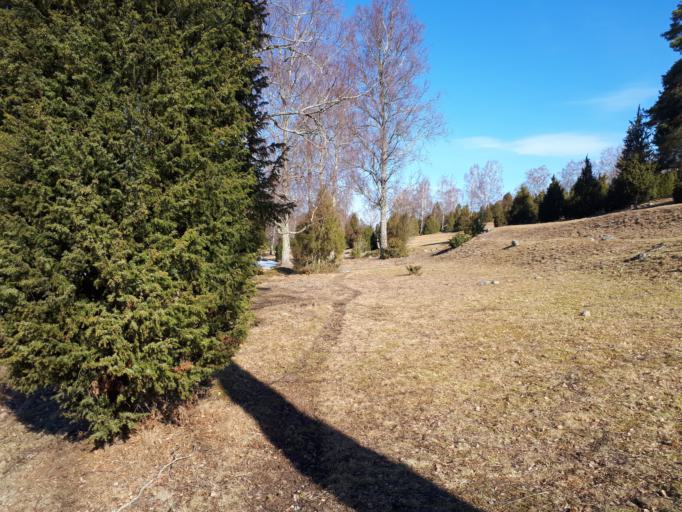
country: SE
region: Soedermanland
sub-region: Flens Kommun
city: Halleforsnas
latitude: 59.0769
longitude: 16.3711
